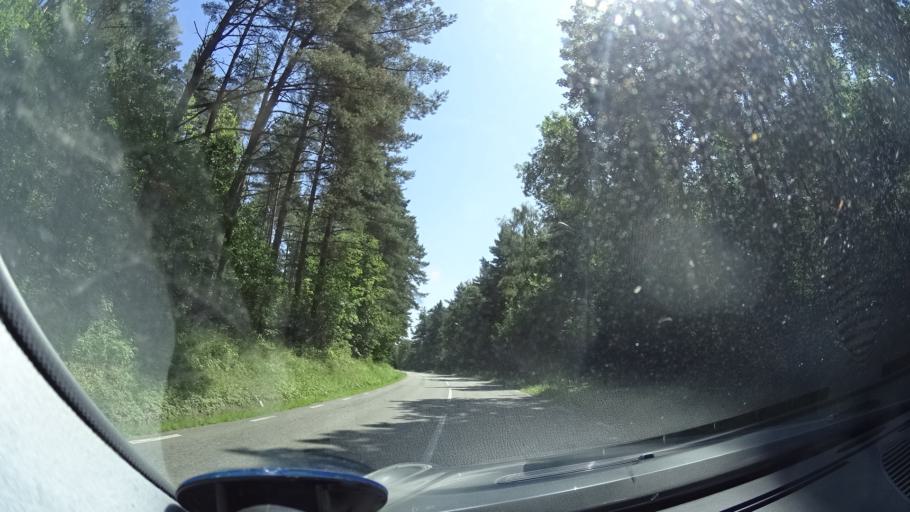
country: SE
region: Skane
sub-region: Kristianstads Kommun
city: Onnestad
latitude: 55.9256
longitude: 13.9704
